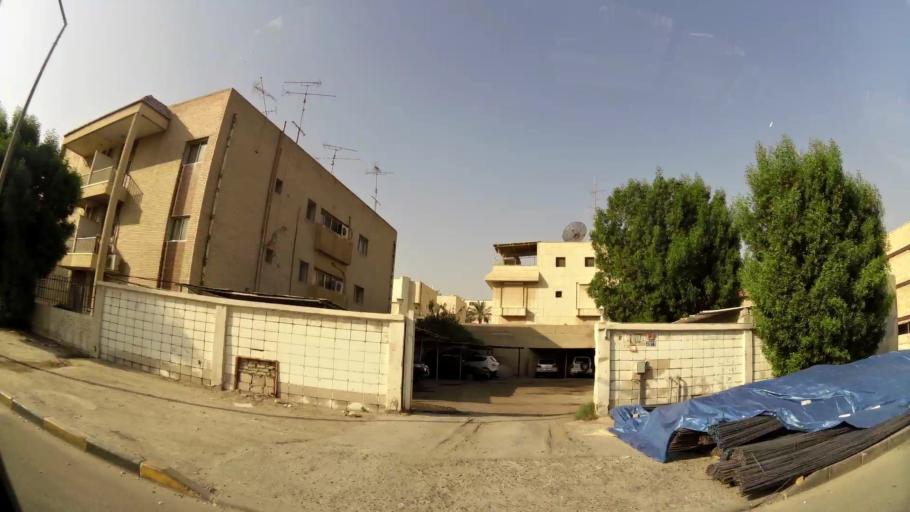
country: KW
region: Muhafazat Hawalli
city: Hawalli
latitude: 29.3229
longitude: 48.0453
